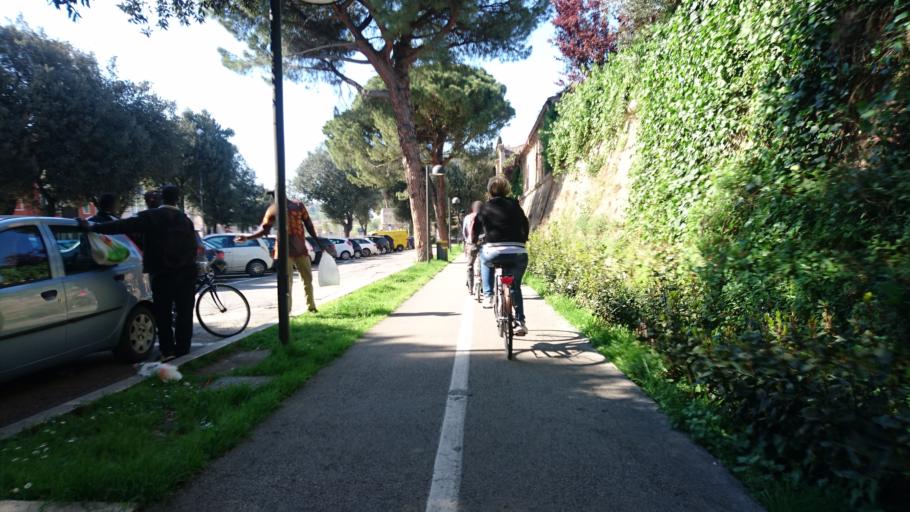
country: IT
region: The Marches
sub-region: Provincia di Pesaro e Urbino
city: Pesaro
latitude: 43.9101
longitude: 12.9047
